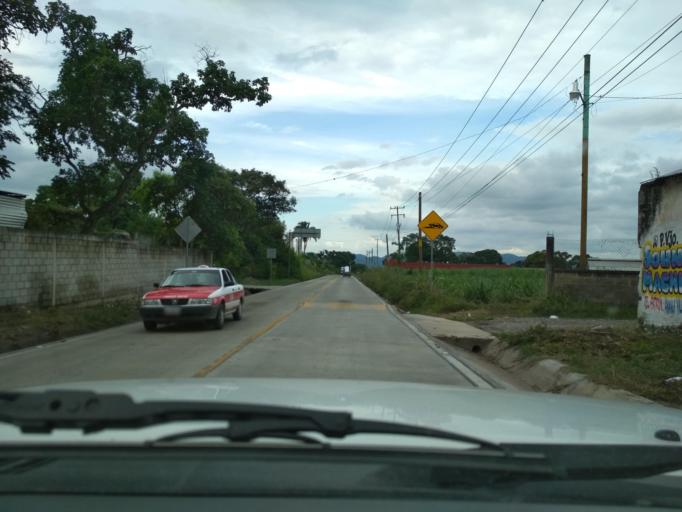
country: MX
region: Veracruz
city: Paraje Nuevo
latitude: 18.8722
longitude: -96.8555
